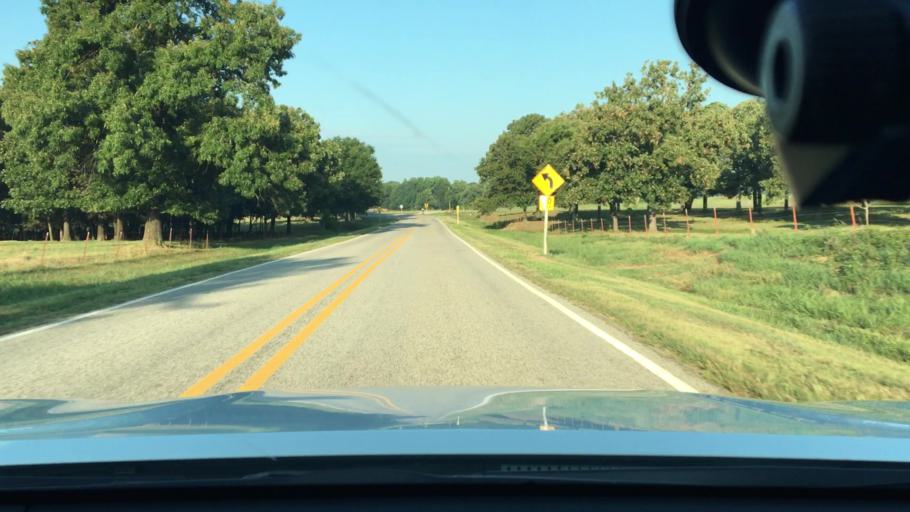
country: US
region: Arkansas
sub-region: Johnson County
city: Coal Hill
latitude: 35.3562
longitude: -93.5635
